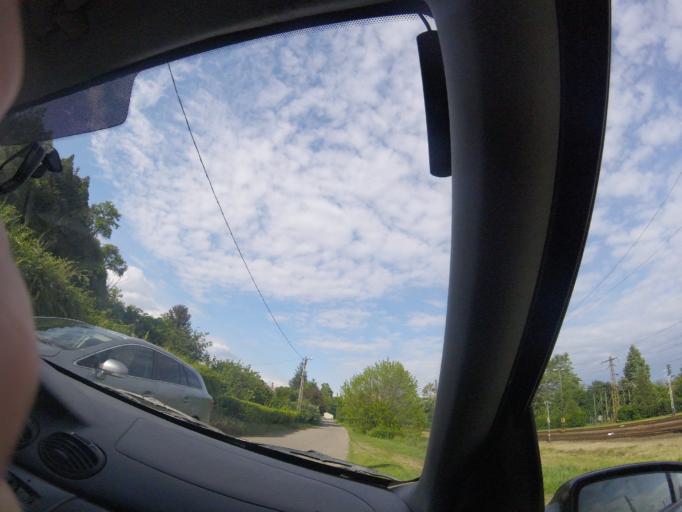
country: HU
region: Borsod-Abauj-Zemplen
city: Tokaj
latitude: 48.1136
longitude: 21.4067
